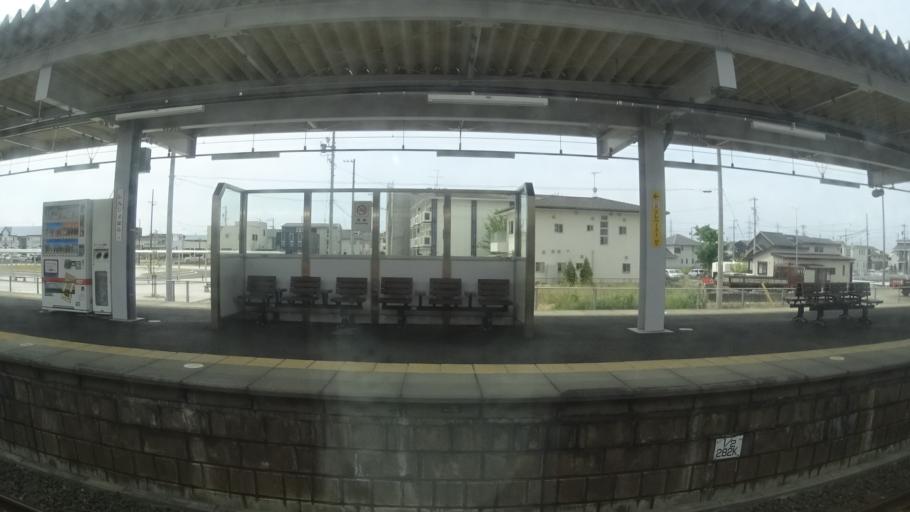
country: JP
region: Shizuoka
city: Kosai-shi
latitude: 34.7233
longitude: 137.4841
